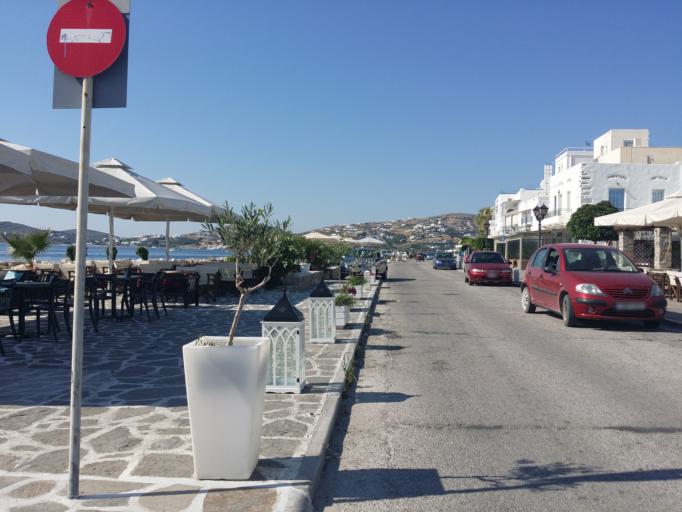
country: GR
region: South Aegean
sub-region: Nomos Kykladon
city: Paros
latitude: 37.0835
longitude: 25.1464
